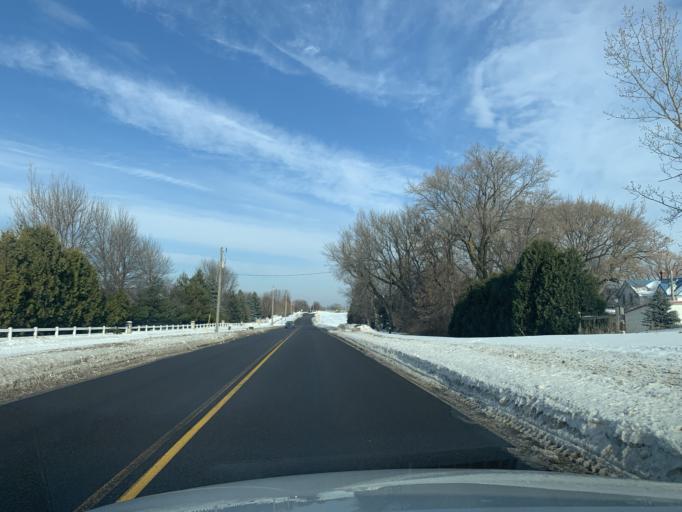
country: US
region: Minnesota
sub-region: Wright County
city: Albertville
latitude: 45.2193
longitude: -93.6441
